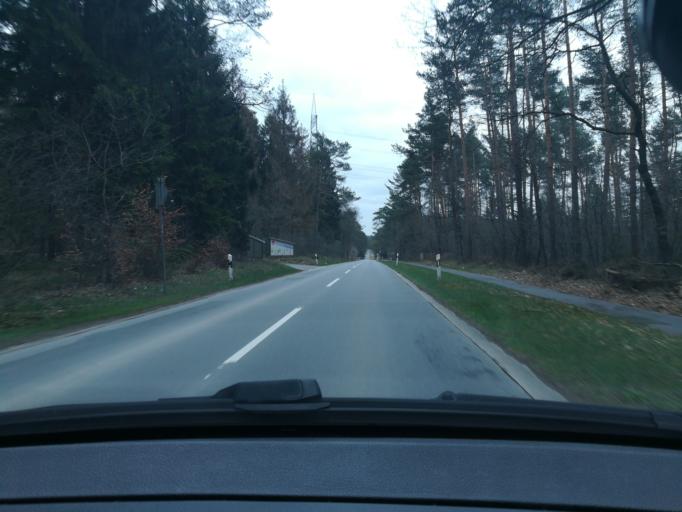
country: DE
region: North Rhine-Westphalia
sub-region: Regierungsbezirk Detmold
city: Oerlinghausen
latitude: 51.9520
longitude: 8.6170
